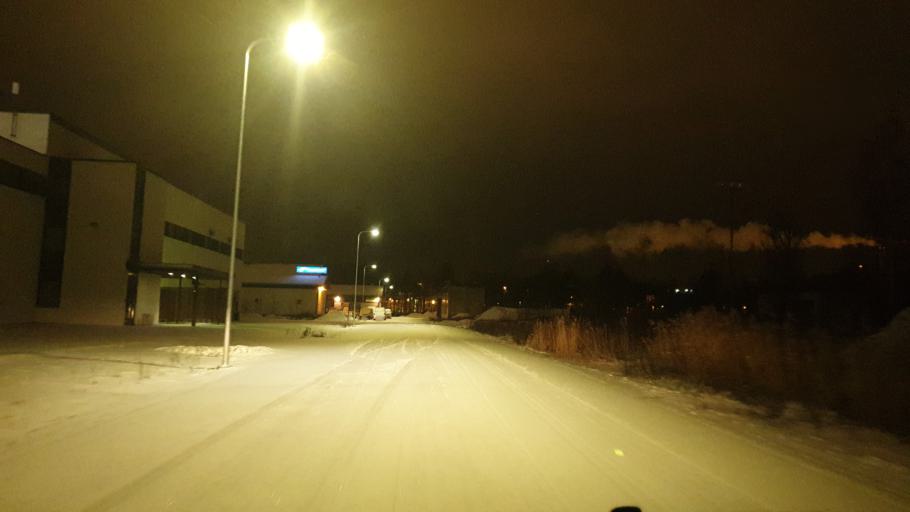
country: FI
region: Northern Ostrobothnia
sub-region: Oulu
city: Oulu
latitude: 64.9951
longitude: 25.4422
